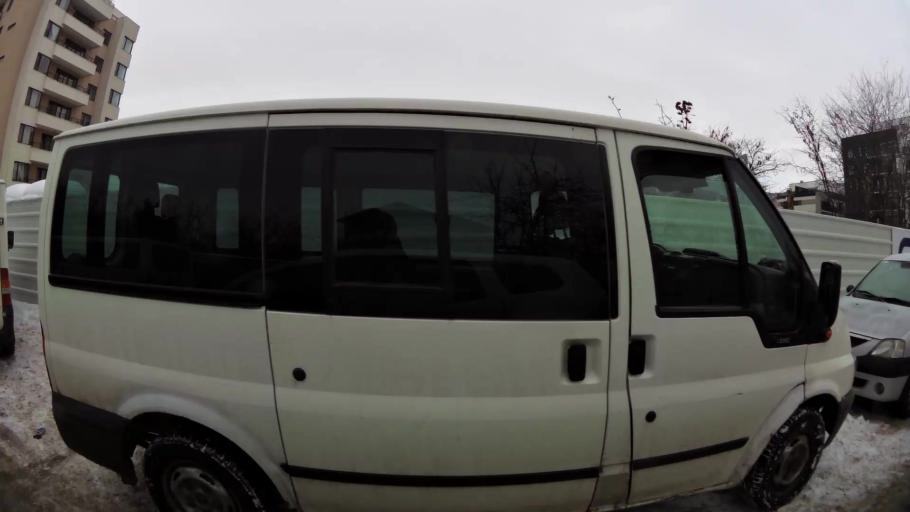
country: RO
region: Ilfov
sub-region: Comuna Otopeni
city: Otopeni
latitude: 44.5129
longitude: 26.1034
